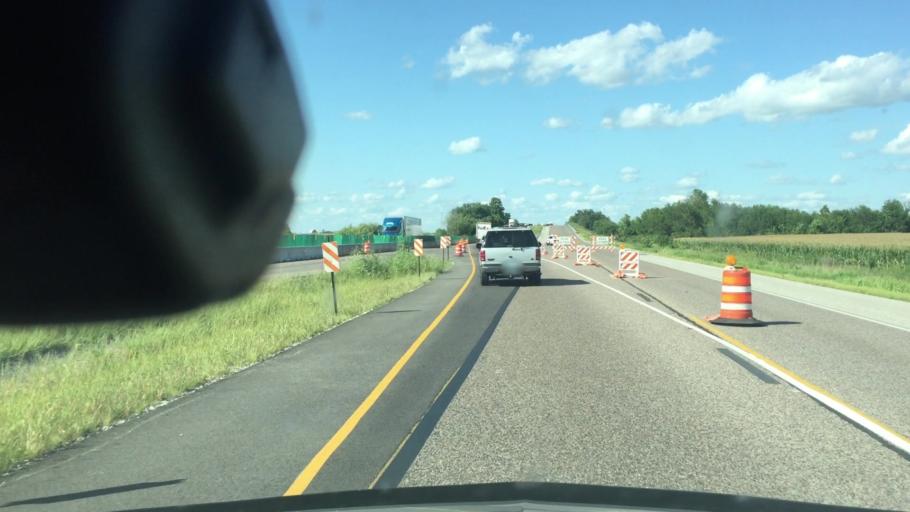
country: US
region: Illinois
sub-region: Madison County
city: Edwardsville
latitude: 38.8200
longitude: -89.8866
